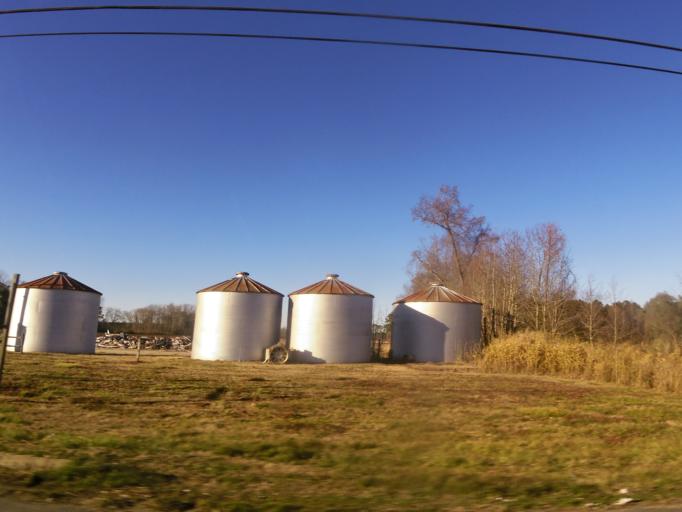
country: US
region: Virginia
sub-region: Isle of Wight County
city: Windsor
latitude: 36.6873
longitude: -76.7607
